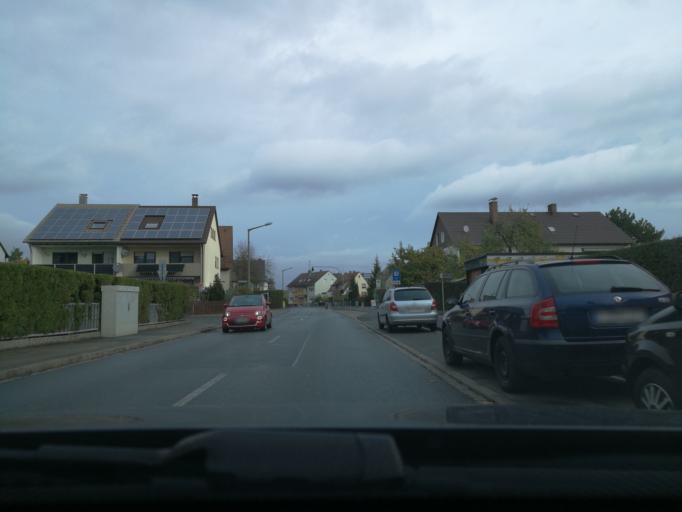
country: DE
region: Bavaria
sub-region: Regierungsbezirk Mittelfranken
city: Furth
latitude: 49.5122
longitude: 10.9785
